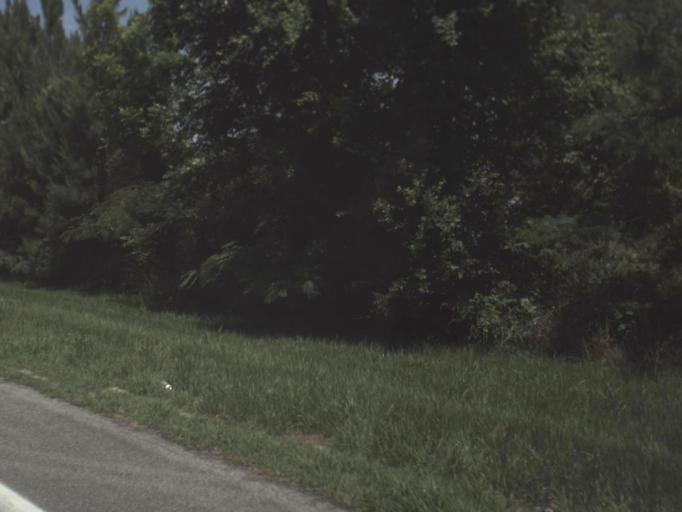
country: US
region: Florida
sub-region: Suwannee County
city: Live Oak
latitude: 30.3208
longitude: -83.0399
